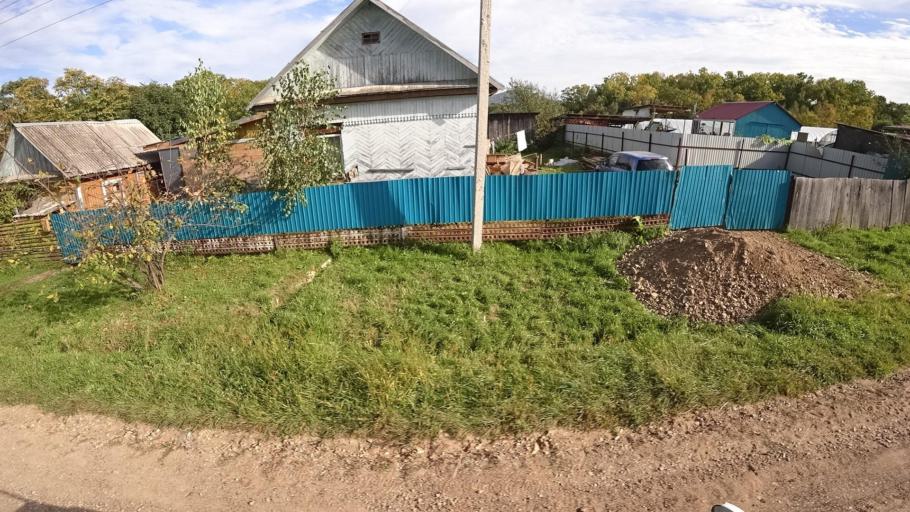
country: RU
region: Primorskiy
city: Dostoyevka
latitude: 44.3012
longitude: 133.4579
